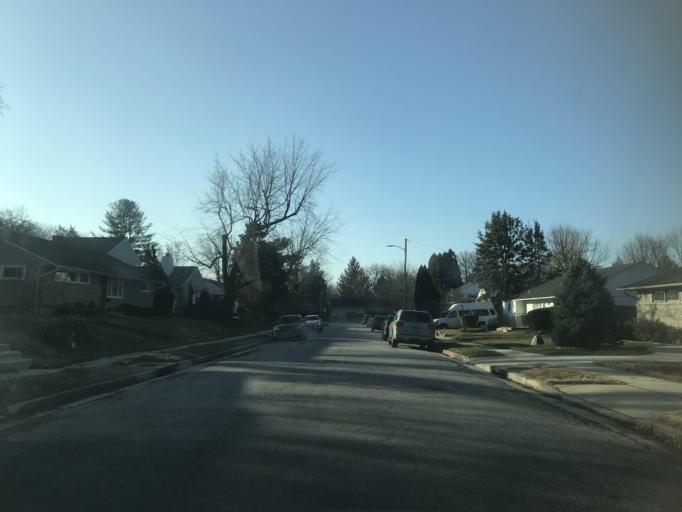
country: US
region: Maryland
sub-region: Baltimore County
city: Towson
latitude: 39.3902
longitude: -76.5940
